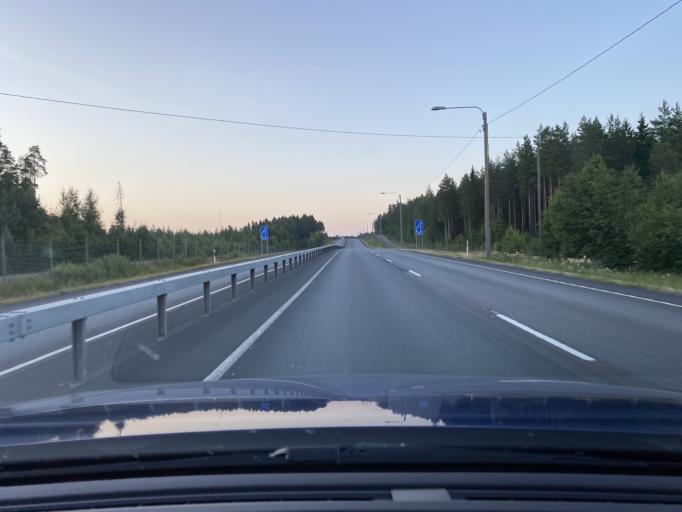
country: FI
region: Pirkanmaa
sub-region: Luoteis-Pirkanmaa
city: Parkano
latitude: 61.8864
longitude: 22.9748
